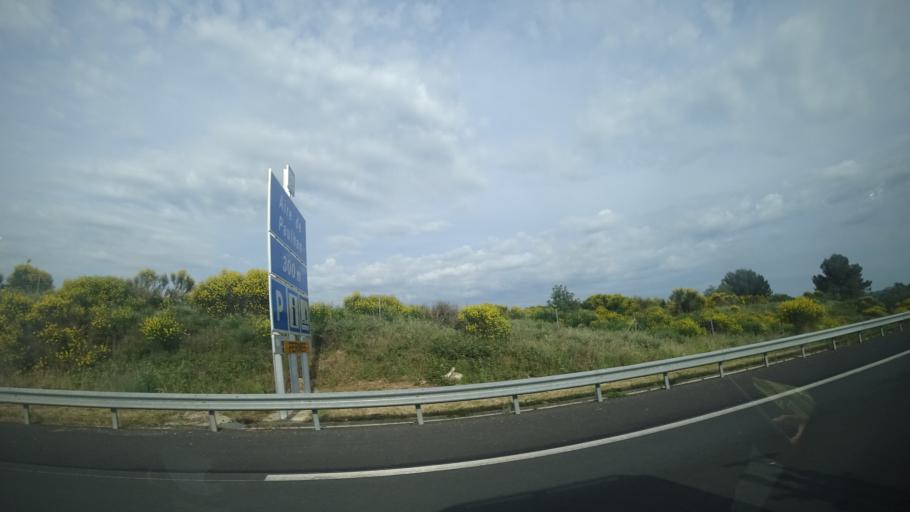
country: FR
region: Languedoc-Roussillon
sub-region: Departement de l'Herault
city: Paulhan
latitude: 43.5355
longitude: 3.4438
